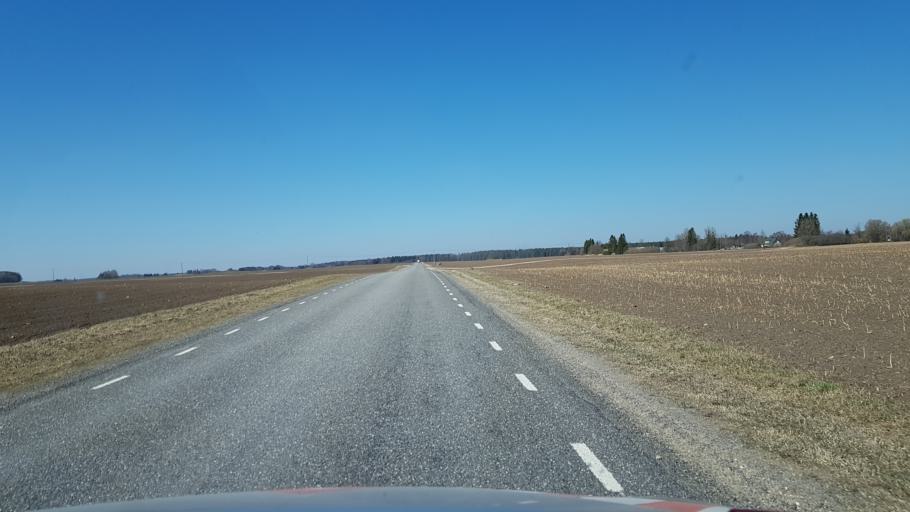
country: EE
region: Laeaene-Virumaa
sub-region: Rakke vald
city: Rakke
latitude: 59.0023
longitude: 26.1933
